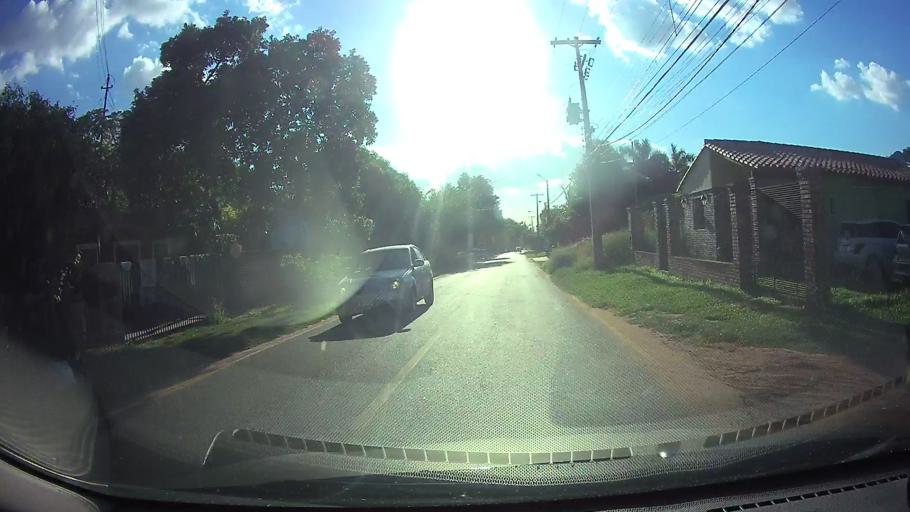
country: PY
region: Central
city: San Lorenzo
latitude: -25.2864
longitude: -57.5102
